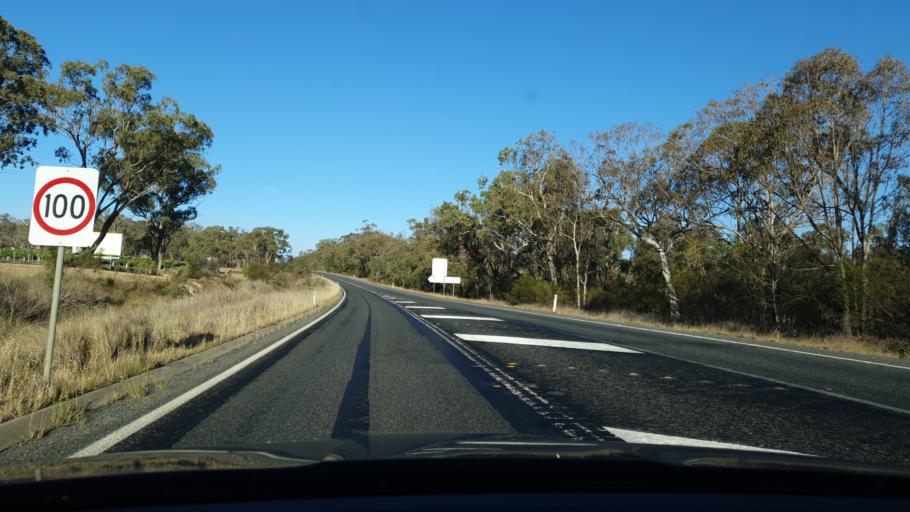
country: AU
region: Queensland
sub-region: Southern Downs
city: Stanthorpe
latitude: -28.6433
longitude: 151.9334
